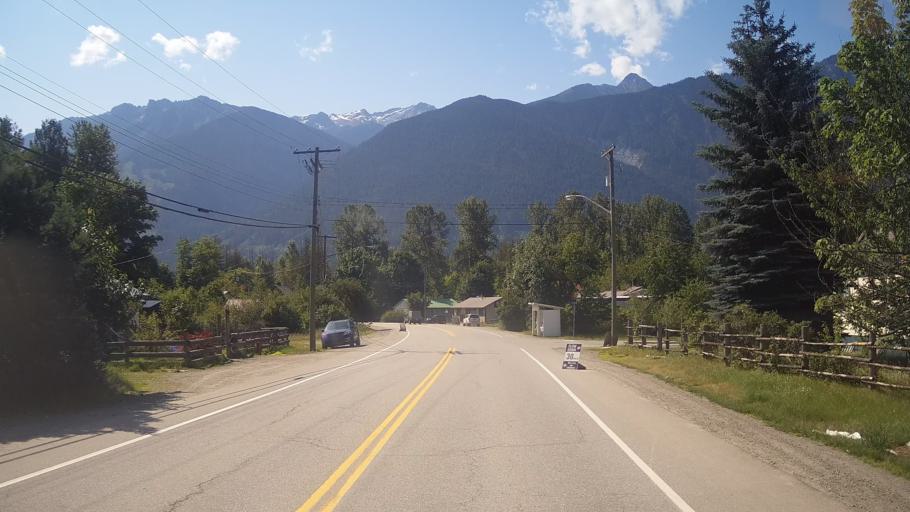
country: CA
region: British Columbia
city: Pemberton
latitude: 50.3188
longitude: -122.7200
